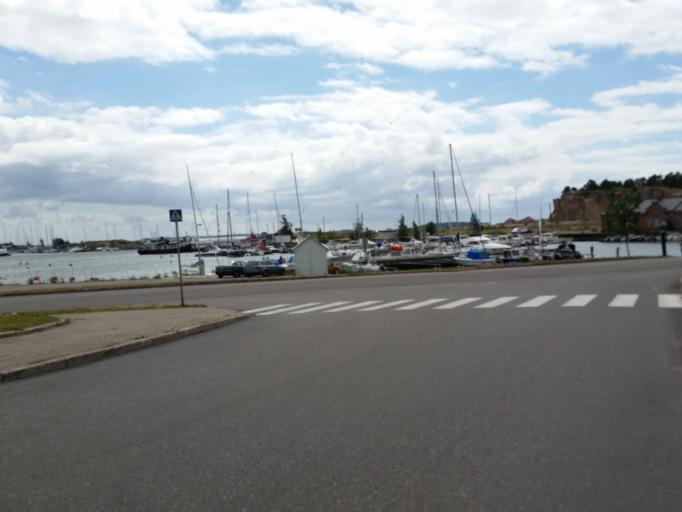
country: FI
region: Uusimaa
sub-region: Raaseporin
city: Hanko
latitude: 59.8218
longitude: 22.9649
